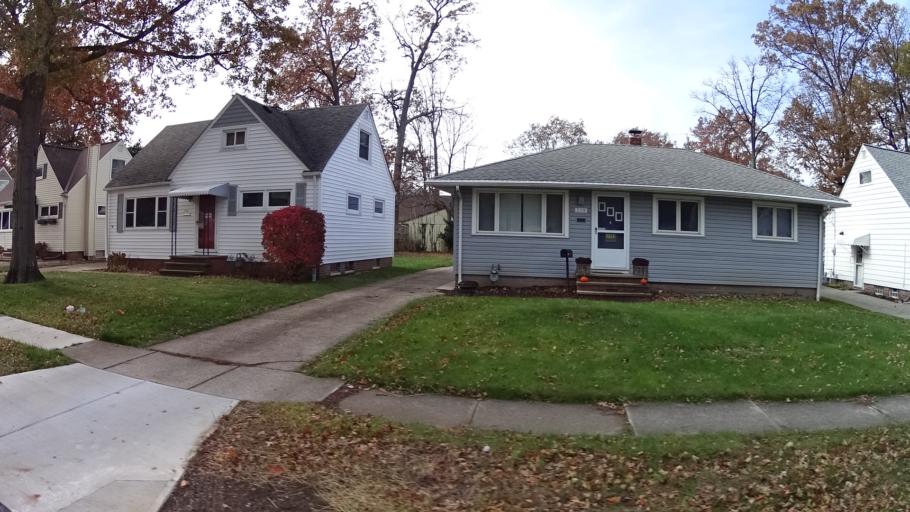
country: US
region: Ohio
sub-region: Lorain County
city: Avon Lake
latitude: 41.5051
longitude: -82.0236
